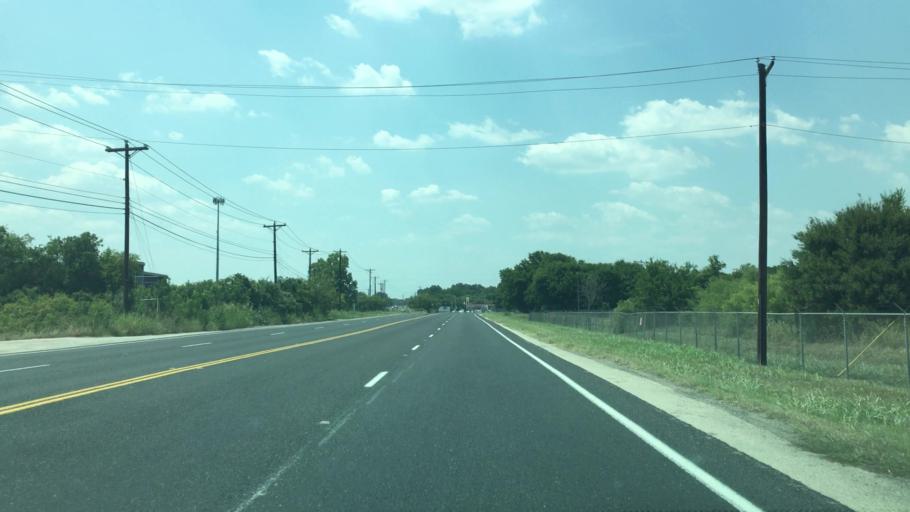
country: US
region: Texas
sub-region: Travis County
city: Austin
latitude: 30.1800
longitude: -97.6843
